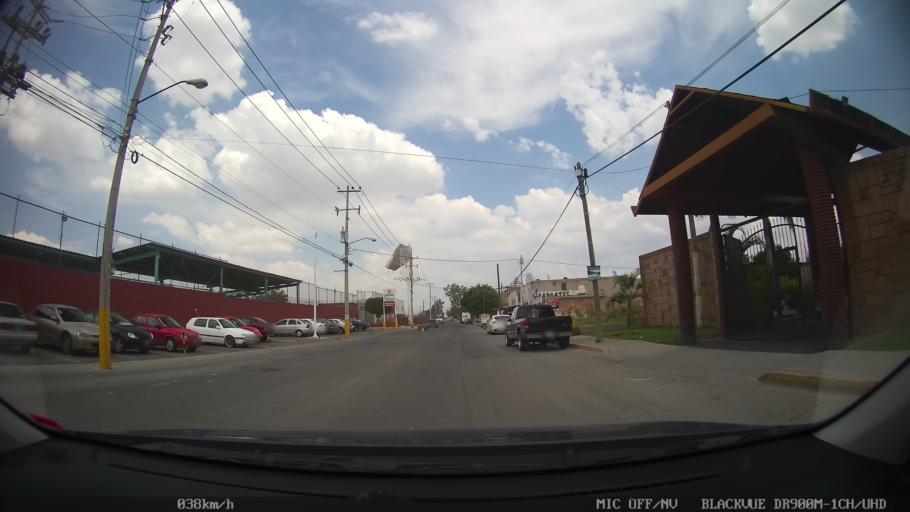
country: MX
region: Jalisco
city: Tonala
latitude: 20.6761
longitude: -103.2347
